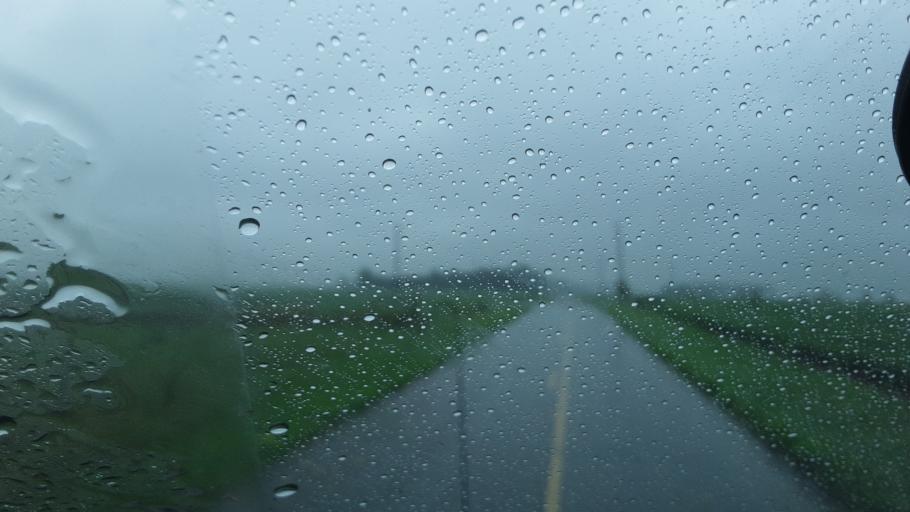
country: US
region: Ohio
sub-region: Mercer County
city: Rockford
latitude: 40.6696
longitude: -84.7958
